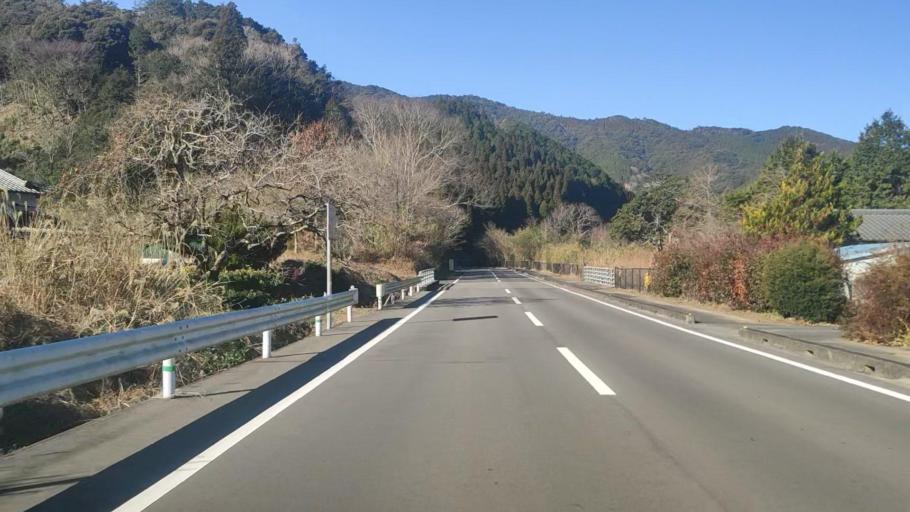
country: JP
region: Miyazaki
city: Nobeoka
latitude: 32.7472
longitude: 131.8080
